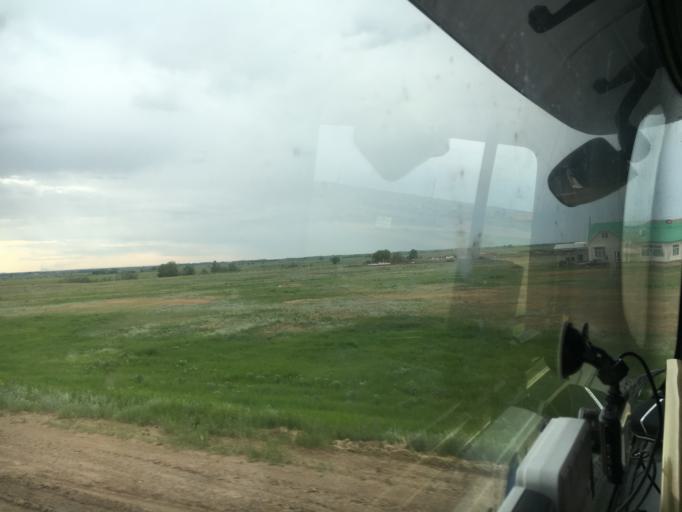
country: KZ
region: Batys Qazaqstan
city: Oral
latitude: 51.1224
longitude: 51.4519
